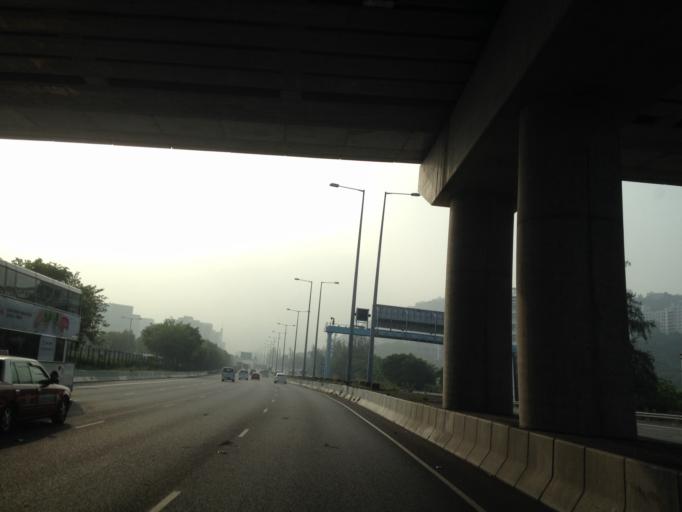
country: HK
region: Tai Po
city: Tai Po
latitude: 22.4300
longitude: 114.2024
